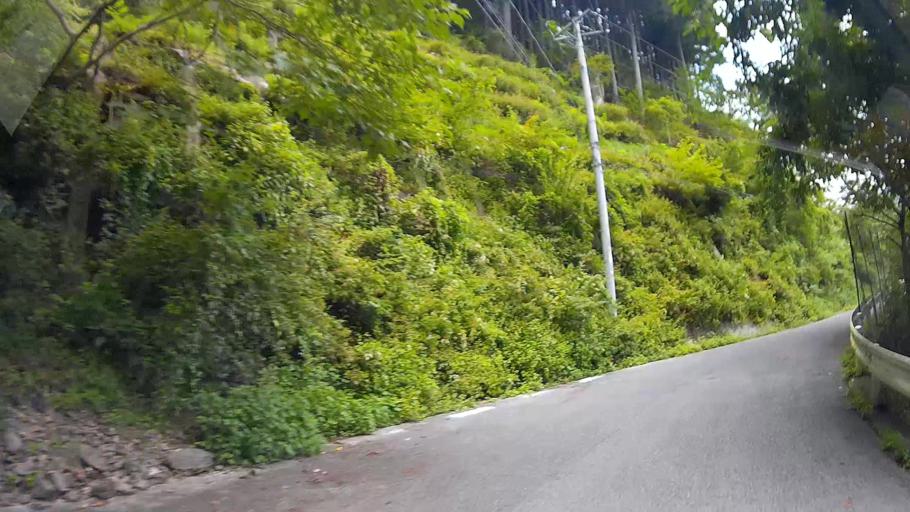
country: JP
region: Saitama
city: Chichibu
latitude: 35.9279
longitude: 139.0650
